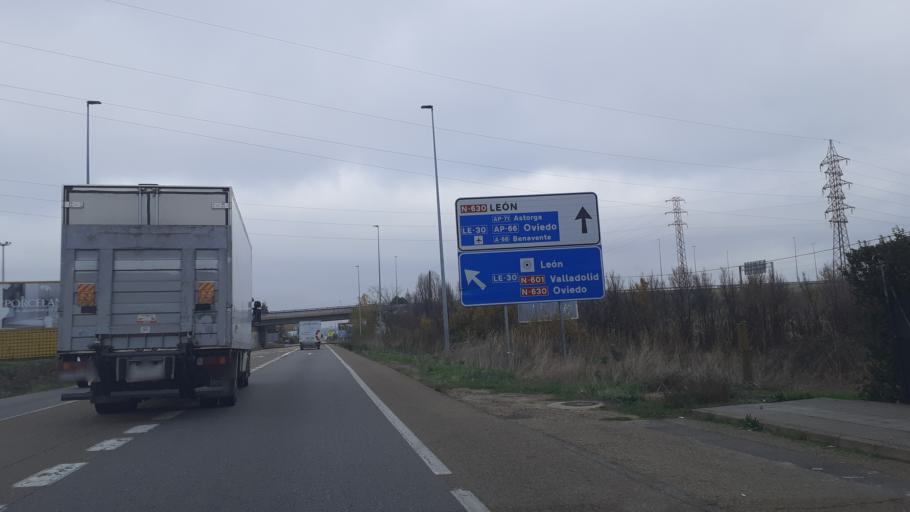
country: ES
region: Castille and Leon
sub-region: Provincia de Leon
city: Leon
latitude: 42.5675
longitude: -5.5824
